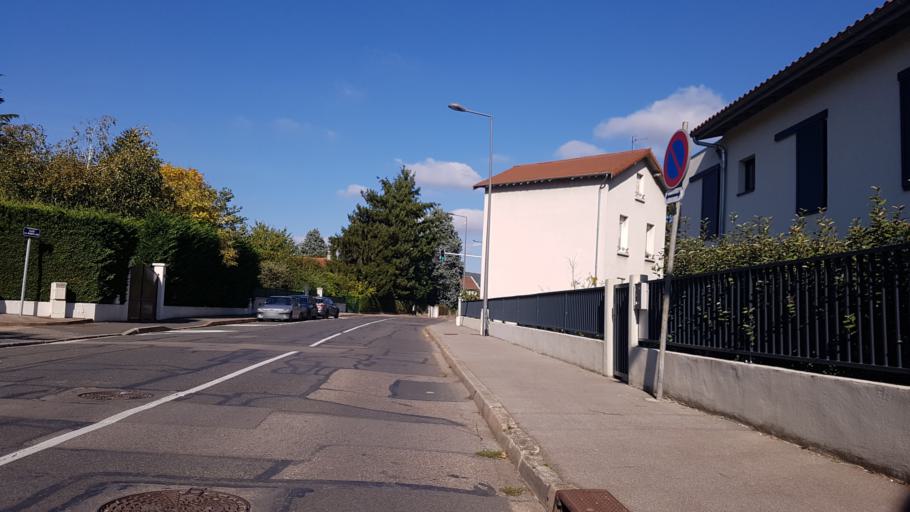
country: FR
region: Rhone-Alpes
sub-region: Departement du Rhone
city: Ecully
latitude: 45.7979
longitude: 4.7851
